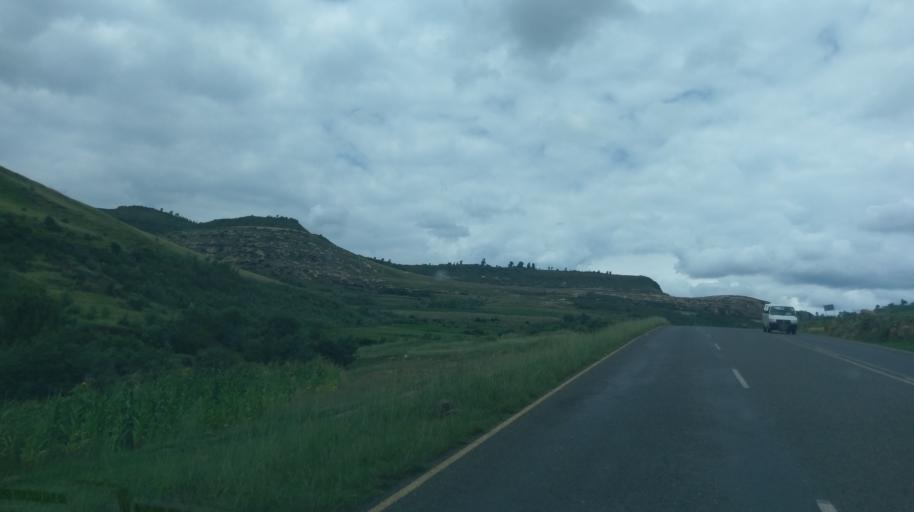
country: LS
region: Leribe
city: Leribe
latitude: -28.9812
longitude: 28.1807
